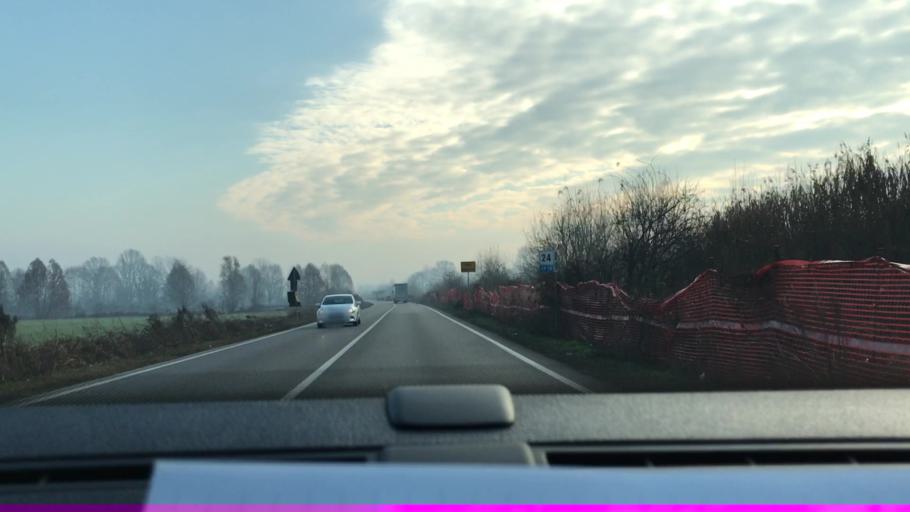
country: IT
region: Lombardy
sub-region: Provincia di Brescia
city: Capriano del Colle
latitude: 45.4857
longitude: 10.1093
